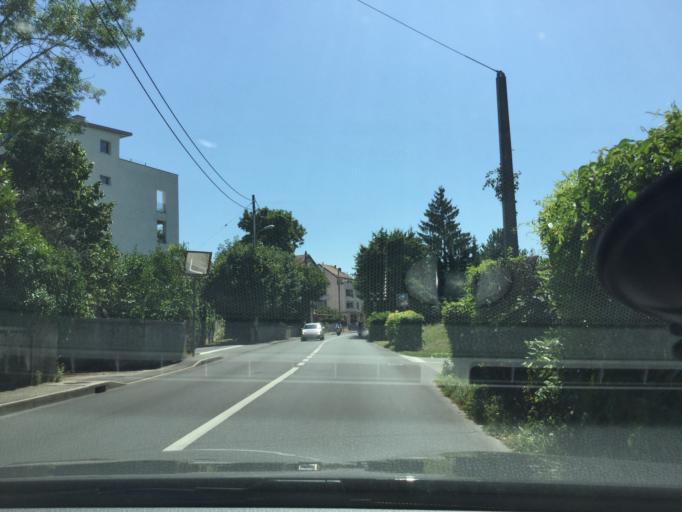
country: CH
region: Geneva
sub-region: Geneva
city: Vandoeuvres
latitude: 46.2421
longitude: 6.1981
